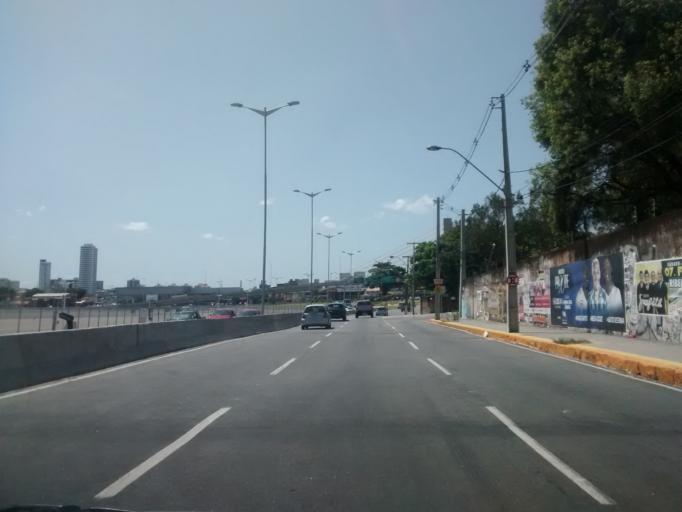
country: BR
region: Rio Grande do Norte
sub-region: Natal
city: Natal
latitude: -5.8251
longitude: -35.2123
